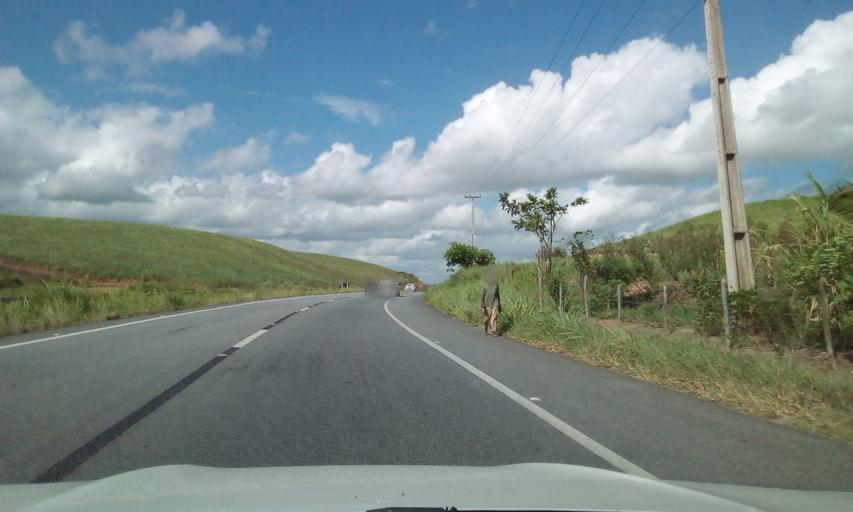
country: BR
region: Alagoas
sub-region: Messias
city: Messias
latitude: -9.3565
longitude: -35.8377
